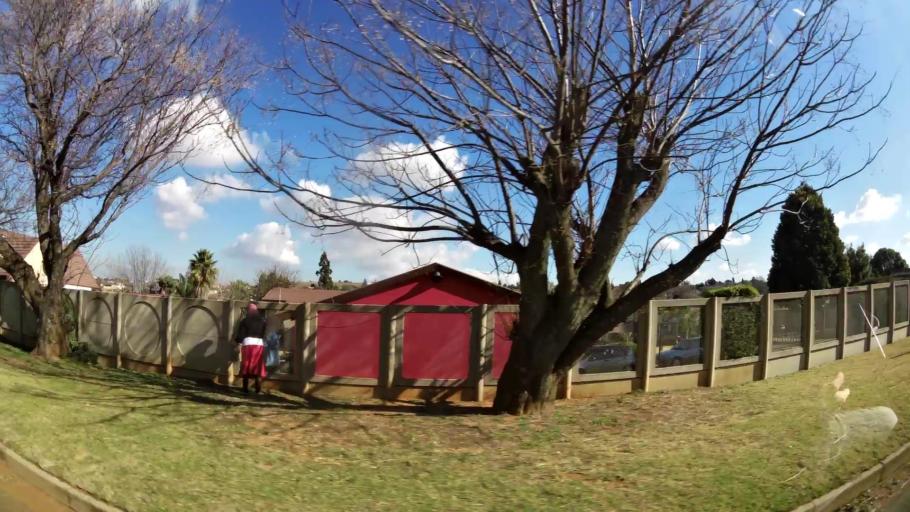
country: ZA
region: Gauteng
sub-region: City of Johannesburg Metropolitan Municipality
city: Roodepoort
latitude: -26.1440
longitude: 27.8216
